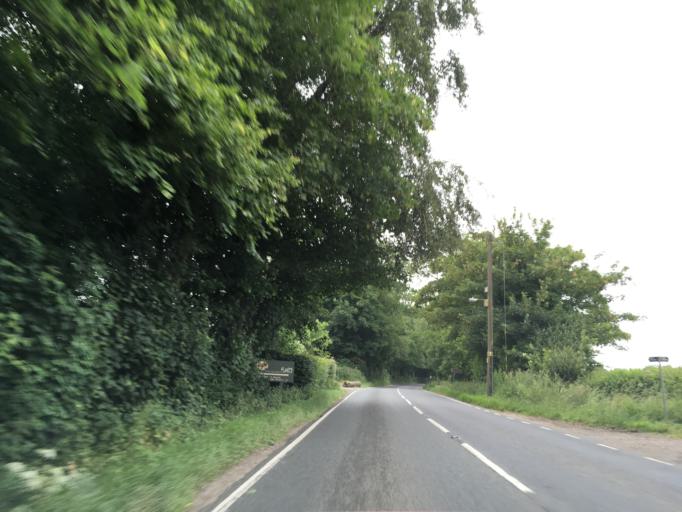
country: GB
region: England
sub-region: Gloucestershire
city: Stonehouse
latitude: 51.7692
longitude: -2.3573
